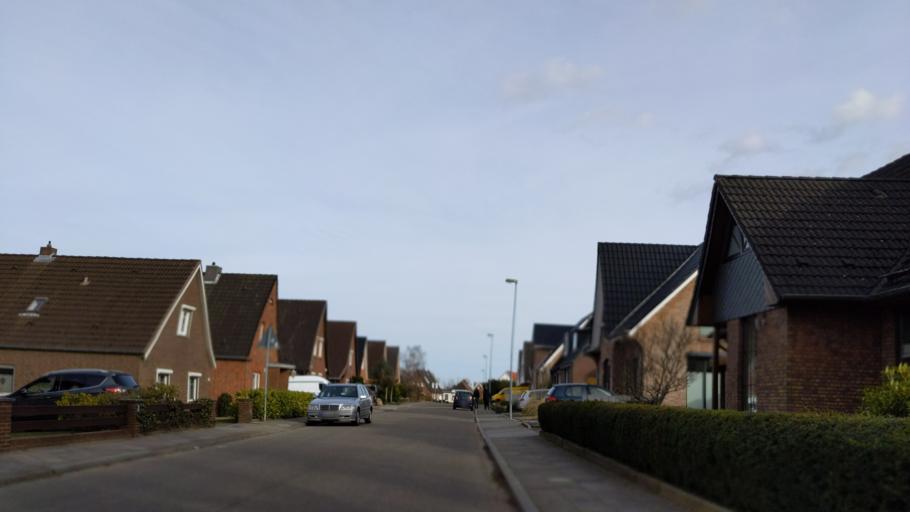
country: DE
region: Mecklenburg-Vorpommern
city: Selmsdorf
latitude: 53.9123
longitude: 10.8216
